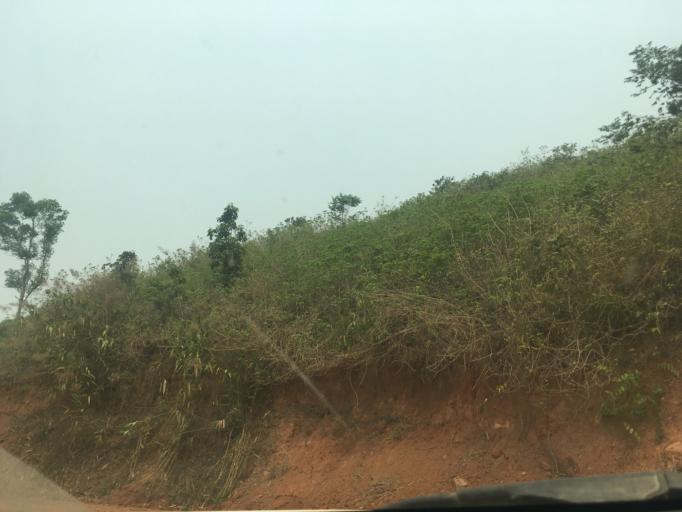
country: VN
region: Huyen Dien Bien
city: Thi Tran Muong Cha
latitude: 21.7143
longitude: 102.8379
